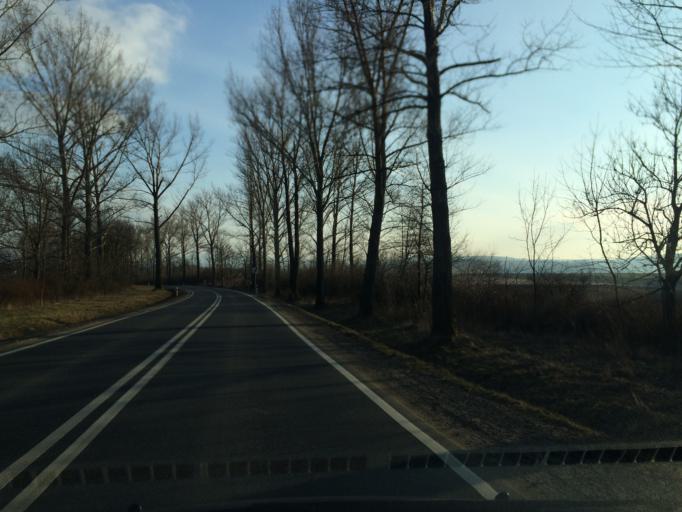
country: PL
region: Lower Silesian Voivodeship
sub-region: Powiat klodzki
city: Miedzylesie
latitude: 50.2277
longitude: 16.6771
